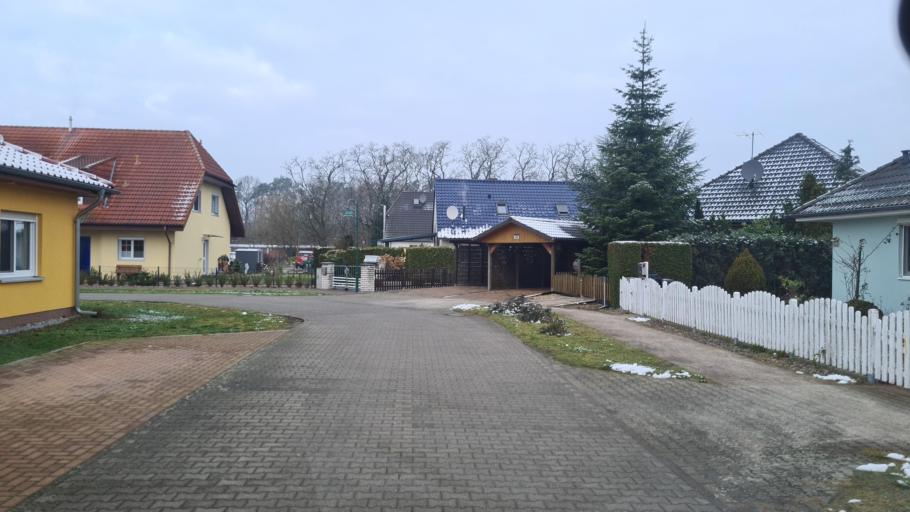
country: DE
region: Brandenburg
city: Spreenhagen
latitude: 52.3476
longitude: 13.8741
